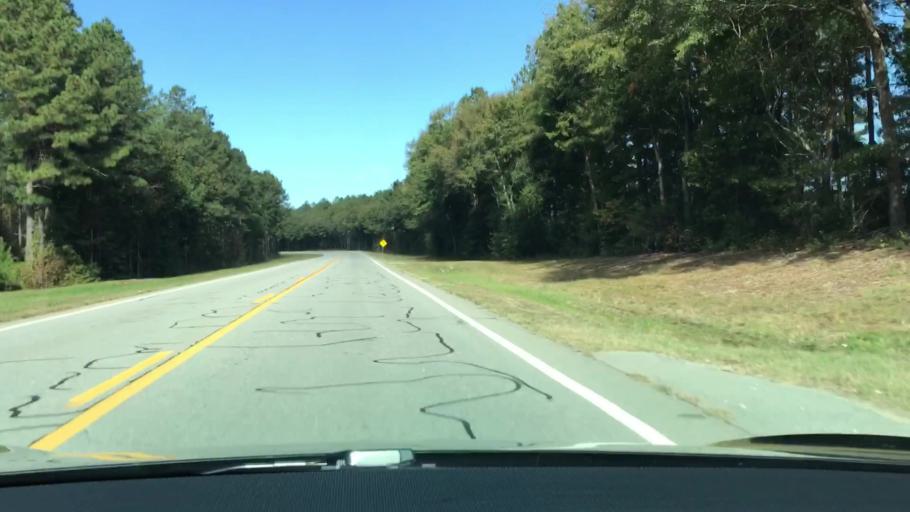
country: US
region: Georgia
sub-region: Warren County
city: Warrenton
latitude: 33.3512
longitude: -82.5858
